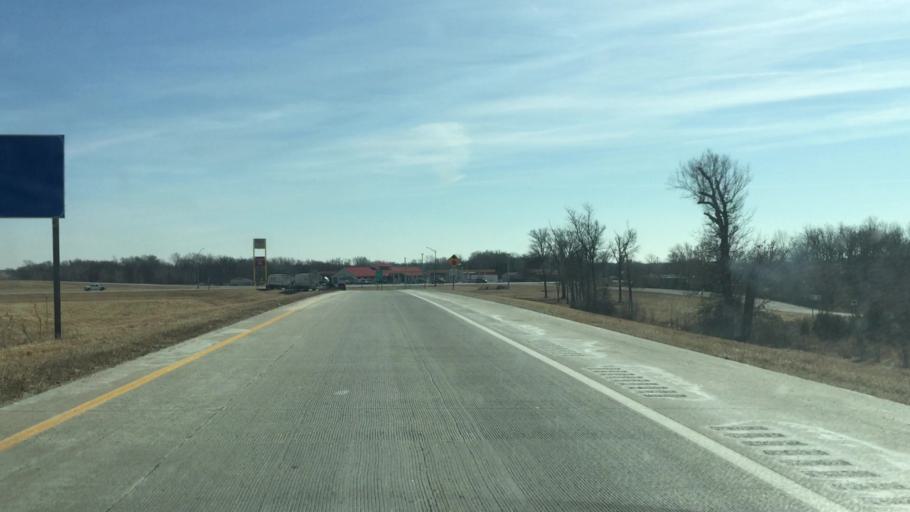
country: US
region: Kansas
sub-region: Labette County
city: Parsons
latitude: 37.3666
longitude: -95.2615
